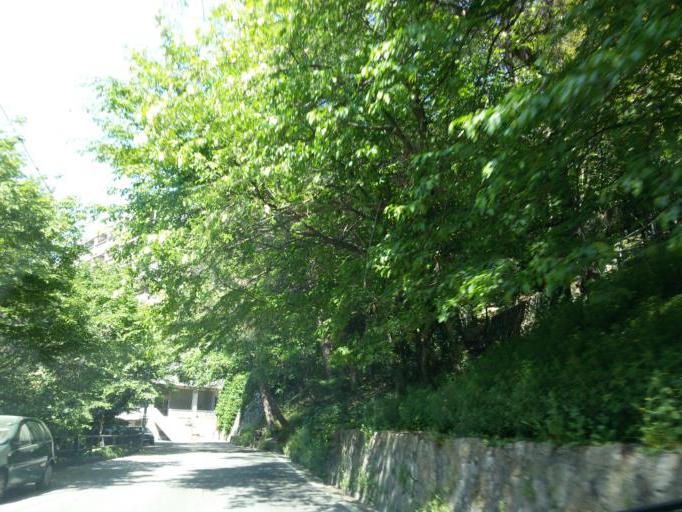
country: IT
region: Liguria
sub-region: Provincia di Genova
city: Genoa
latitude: 44.4232
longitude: 8.9616
